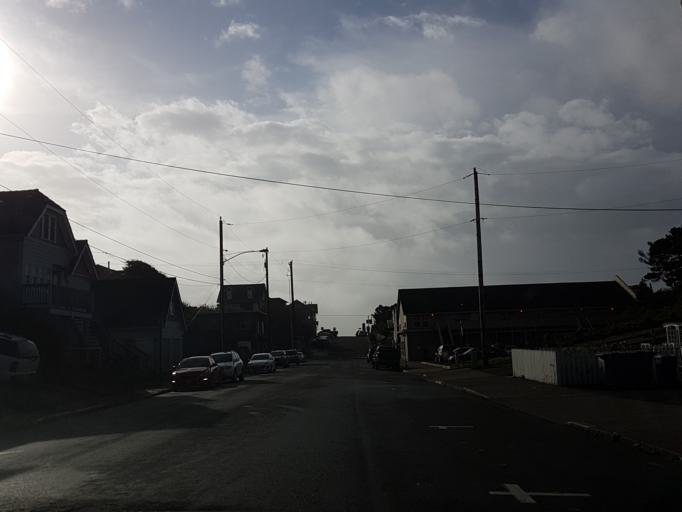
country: US
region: Oregon
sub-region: Lincoln County
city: Newport
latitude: 44.6384
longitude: -124.0593
